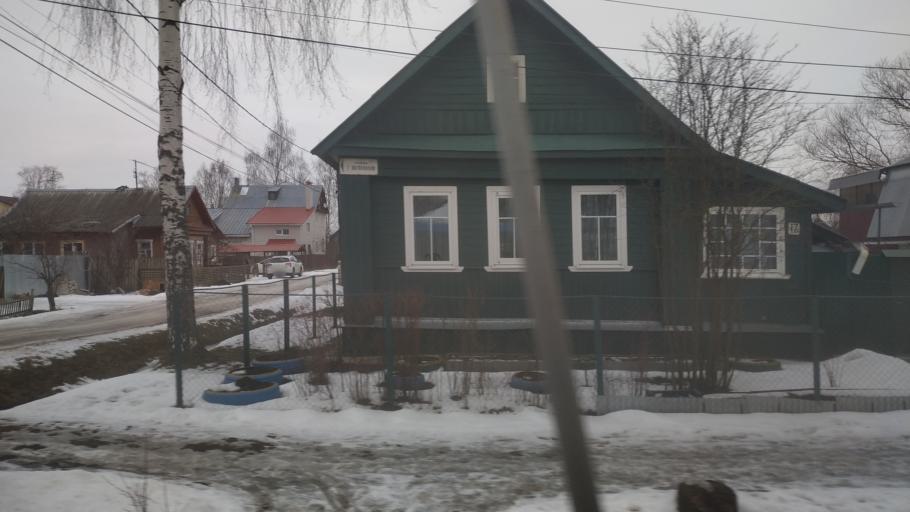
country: RU
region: Tverskaya
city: Tver
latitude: 56.8903
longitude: 35.8535
